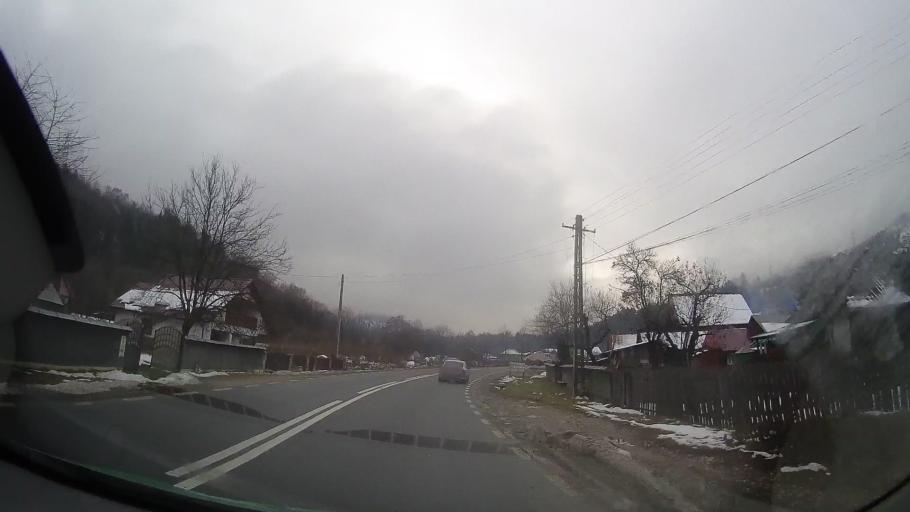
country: RO
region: Neamt
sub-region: Comuna Bicazu Ardelean
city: Bicazu Ardelean
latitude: 46.8649
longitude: 25.9407
